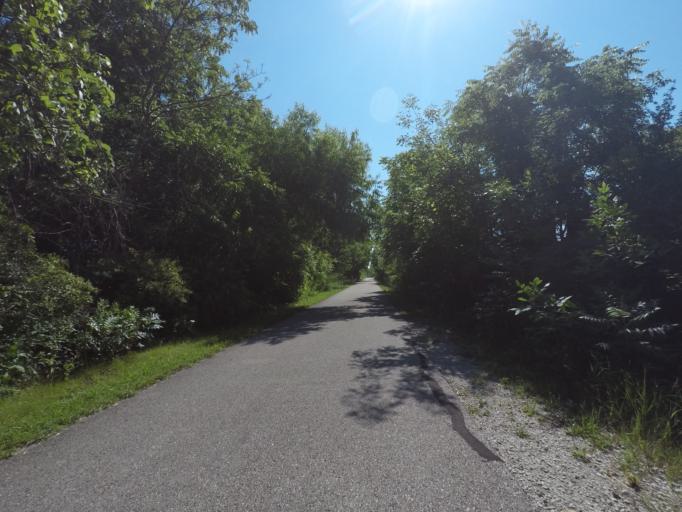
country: US
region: Wisconsin
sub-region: Milwaukee County
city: West Allis
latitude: 43.0247
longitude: -88.0047
